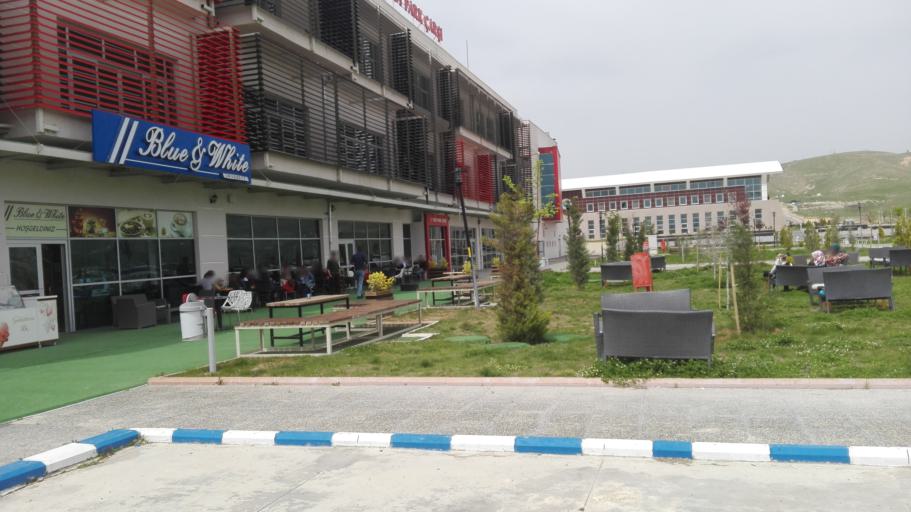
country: TR
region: Batman
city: Oymatas
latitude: 37.7885
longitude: 41.0653
